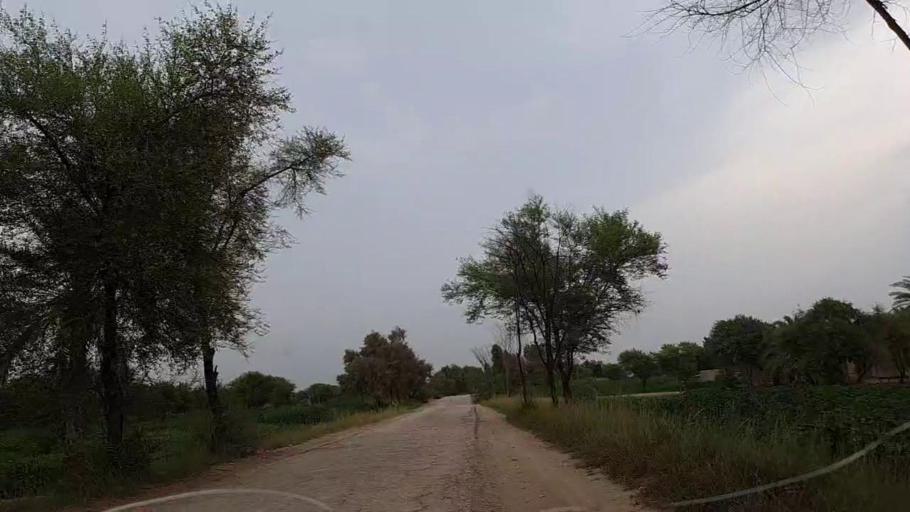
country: PK
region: Sindh
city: Mirpur Mathelo
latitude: 27.8440
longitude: 69.6248
